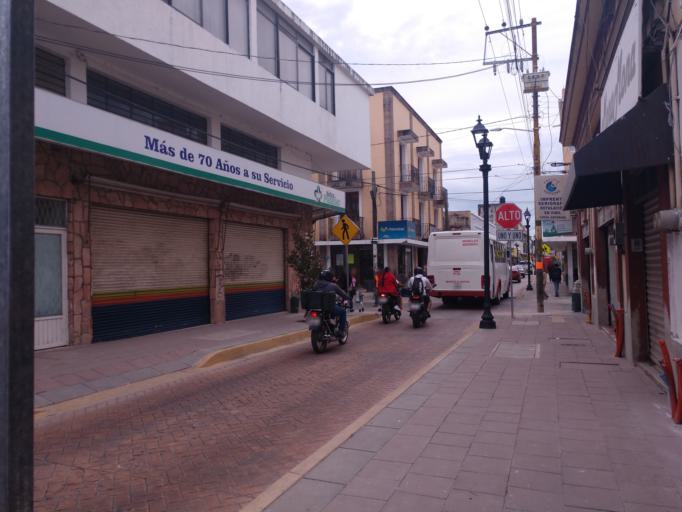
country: MX
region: Nayarit
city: Tepic
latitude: 21.5141
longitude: -104.8932
